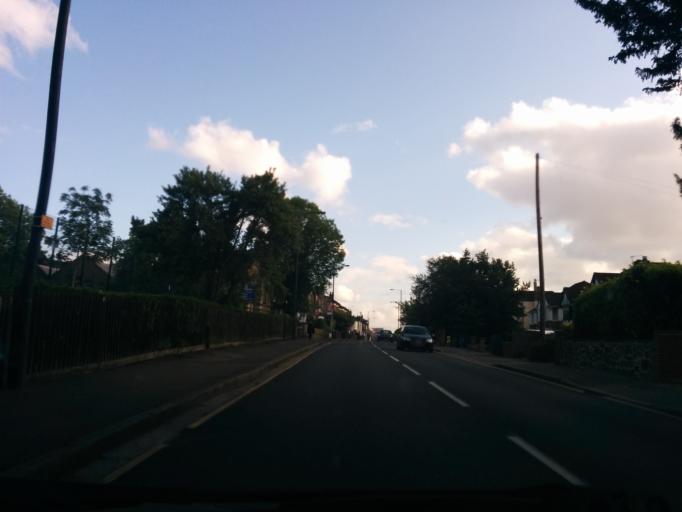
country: GB
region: England
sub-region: Greater London
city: Harrow on the Hill
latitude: 51.5714
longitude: -0.3456
